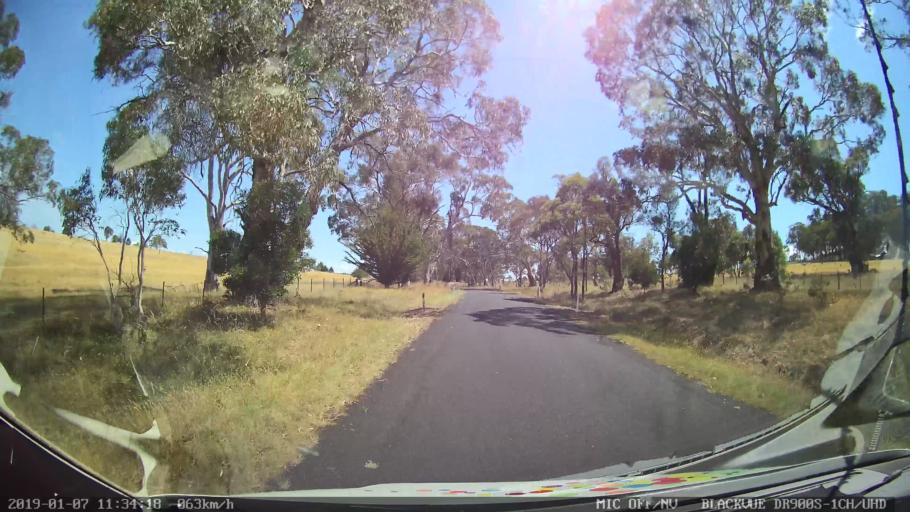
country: AU
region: New South Wales
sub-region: Armidale Dumaresq
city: Armidale
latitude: -30.3912
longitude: 151.5591
